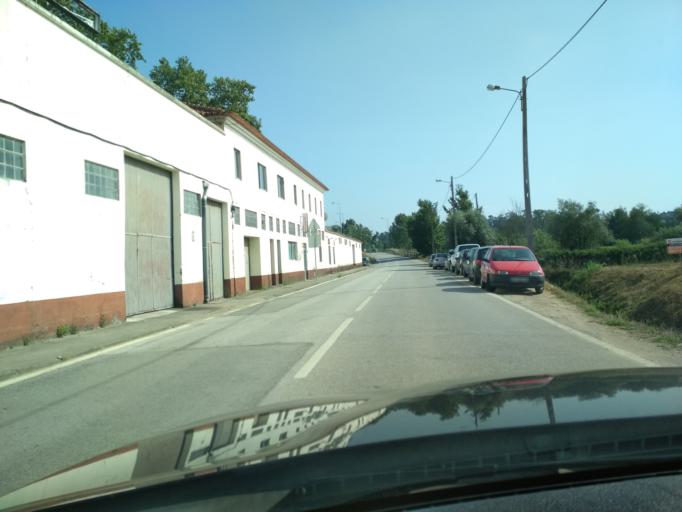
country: PT
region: Aveiro
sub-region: Mealhada
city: Mealhada
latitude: 40.3695
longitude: -8.4544
